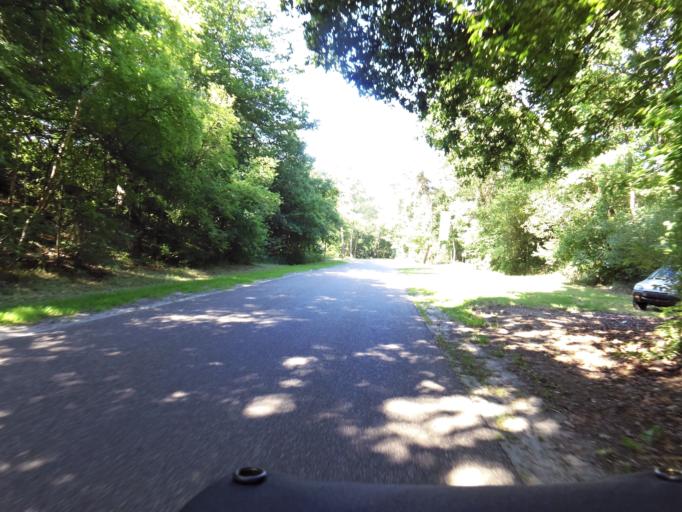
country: NL
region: Overijssel
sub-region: Gemeente Twenterand
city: Den Ham
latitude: 52.4858
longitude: 6.4202
